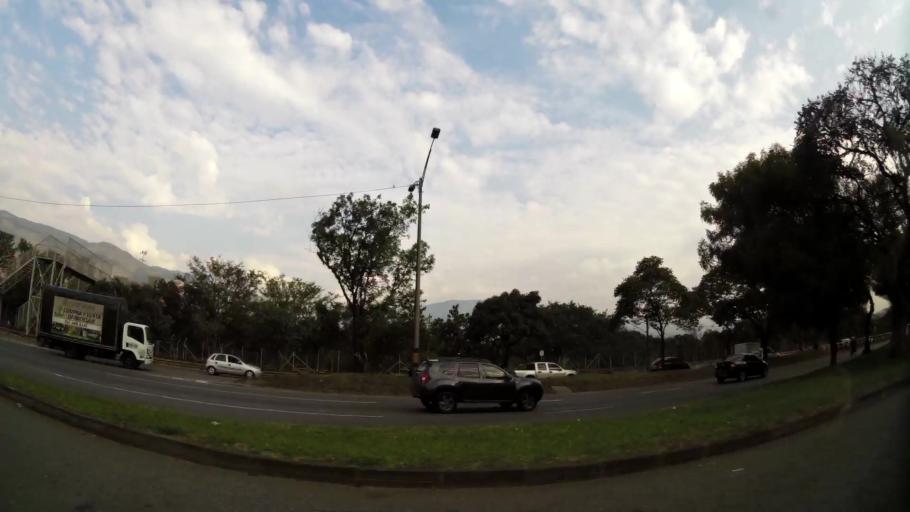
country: CO
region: Antioquia
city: Medellin
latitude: 6.2603
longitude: -75.5748
